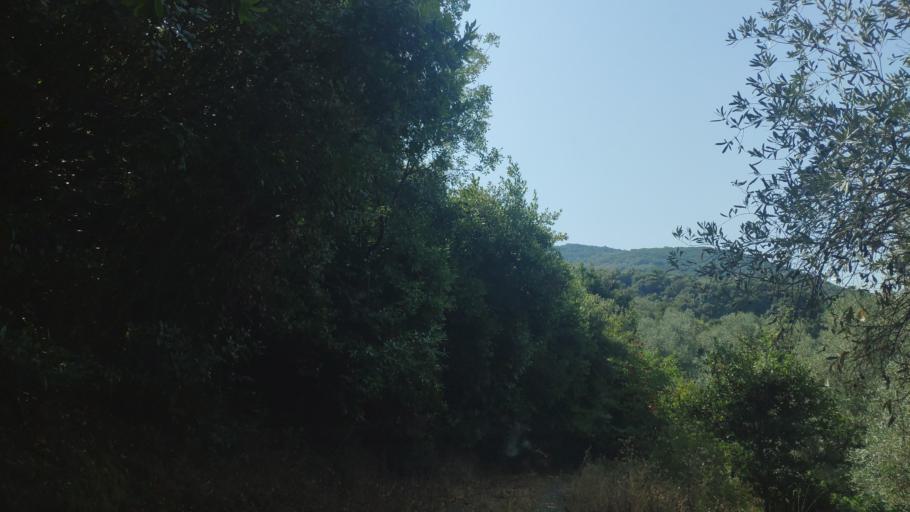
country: GR
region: West Greece
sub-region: Nomos Aitolias kai Akarnanias
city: Fitiai
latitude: 38.7343
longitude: 21.1815
